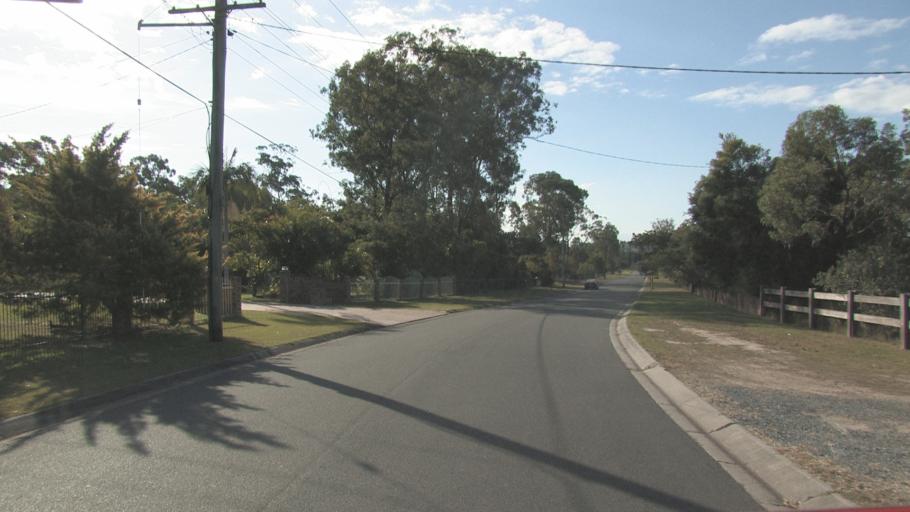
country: AU
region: Queensland
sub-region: Logan
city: Windaroo
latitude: -27.7578
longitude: 153.1916
